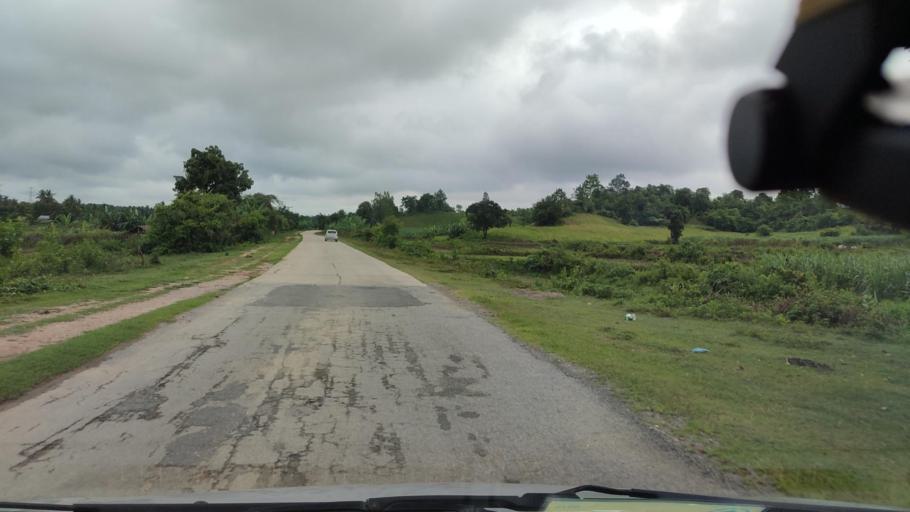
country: MM
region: Mandalay
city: Nay Pyi Taw
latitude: 19.9410
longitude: 95.9798
